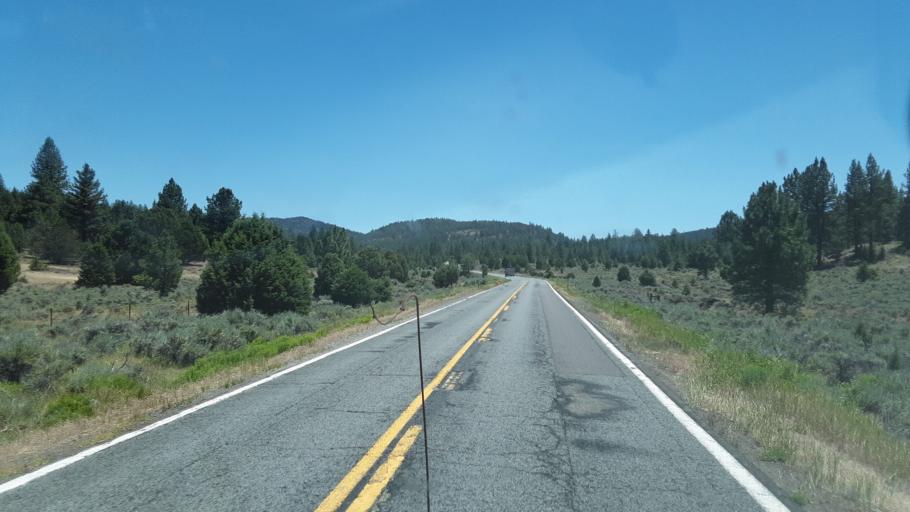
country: US
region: California
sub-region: Modoc County
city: Alturas
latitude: 40.9955
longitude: -120.8072
